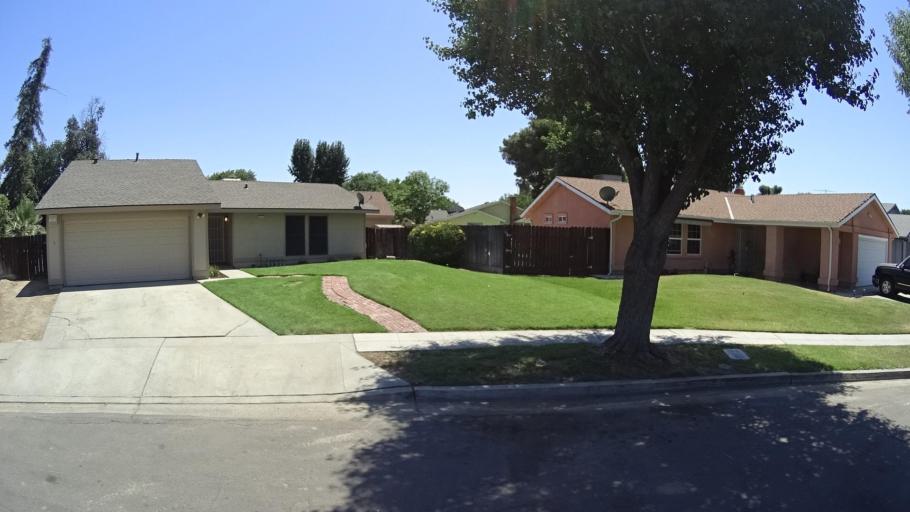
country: US
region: California
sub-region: Fresno County
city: Sunnyside
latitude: 36.7195
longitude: -119.7334
